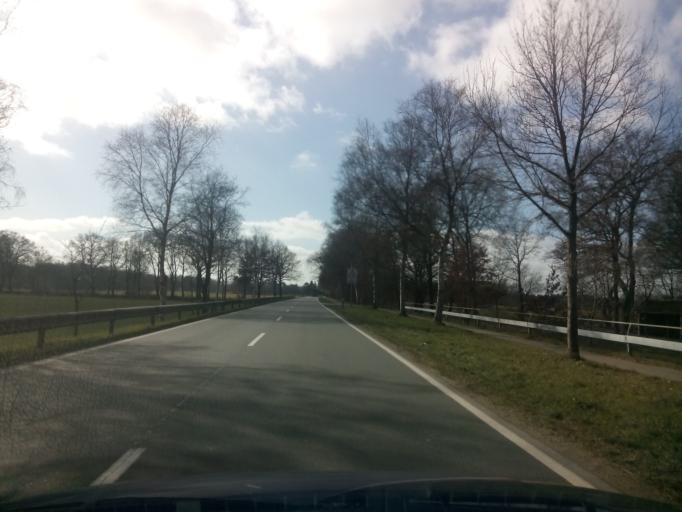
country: DE
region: Lower Saxony
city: Worpswede
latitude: 53.2189
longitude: 8.9077
